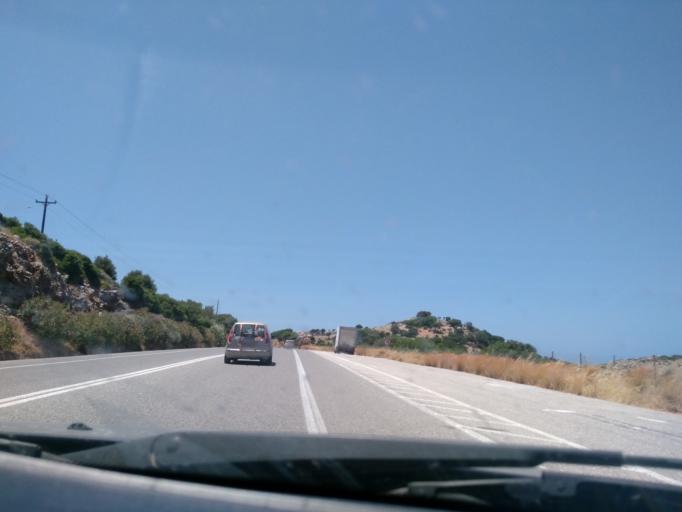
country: GR
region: Crete
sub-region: Nomos Rethymnis
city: Zoniana
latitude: 35.4078
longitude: 24.8275
